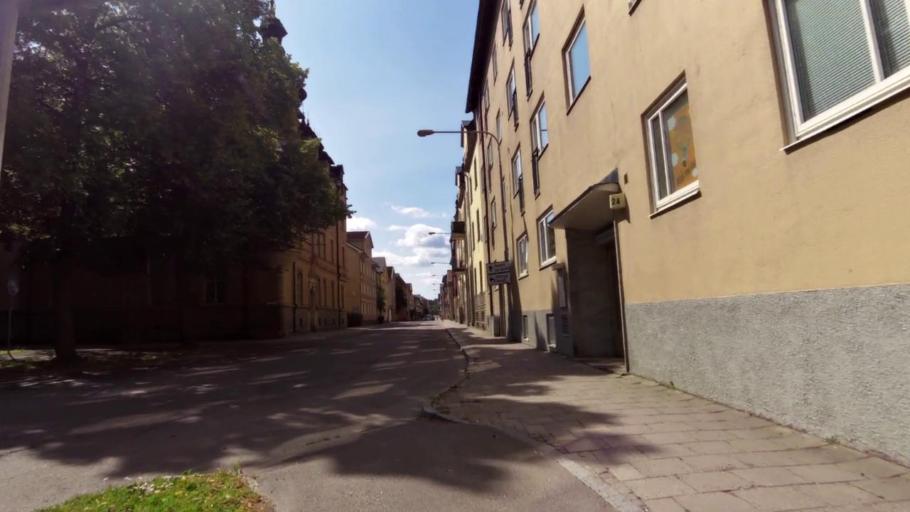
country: SE
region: OEstergoetland
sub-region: Linkopings Kommun
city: Linkoping
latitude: 58.4145
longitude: 15.6274
